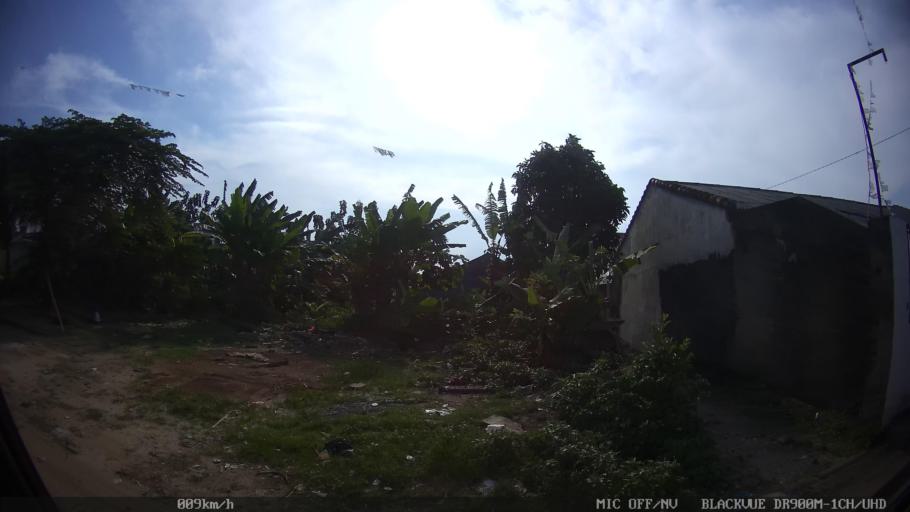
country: ID
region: Lampung
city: Kedaton
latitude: -5.3733
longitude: 105.2363
